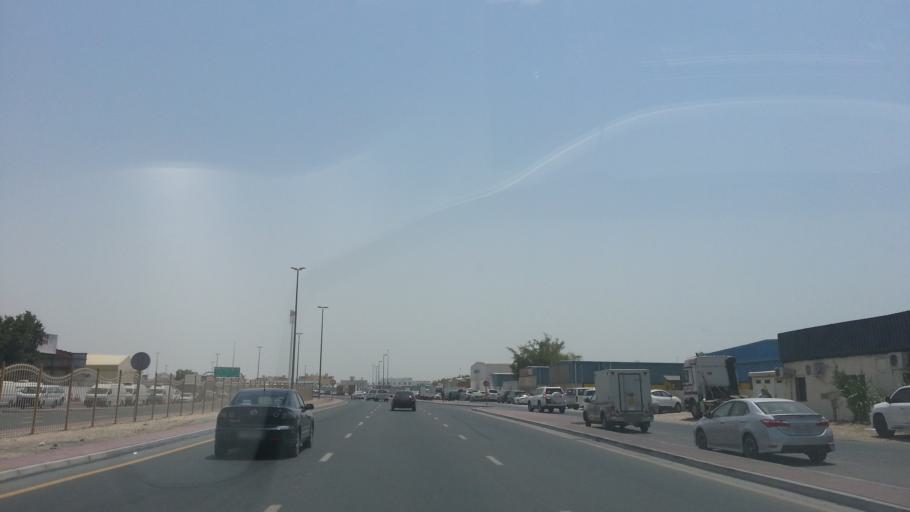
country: AE
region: Dubai
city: Dubai
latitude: 25.1161
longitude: 55.2212
